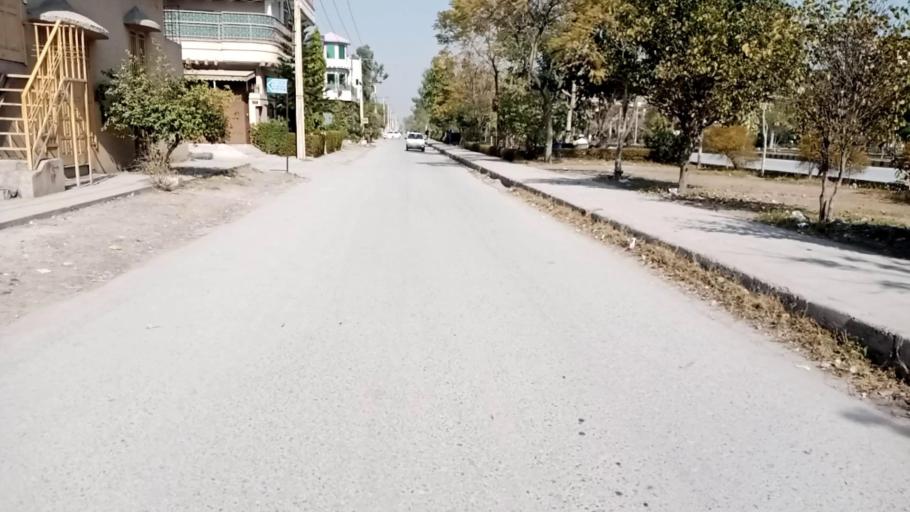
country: PK
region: Khyber Pakhtunkhwa
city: Peshawar
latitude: 33.9531
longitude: 71.4326
